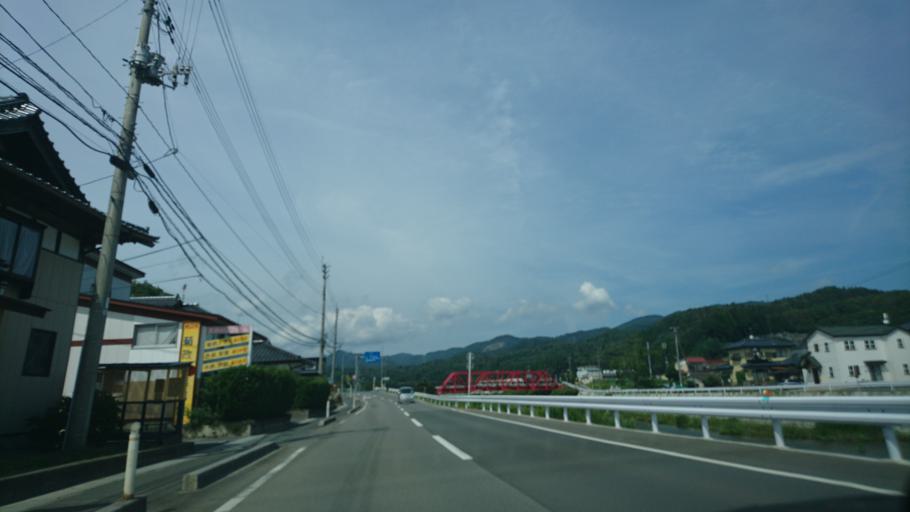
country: JP
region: Iwate
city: Ofunato
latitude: 38.9257
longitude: 141.5829
